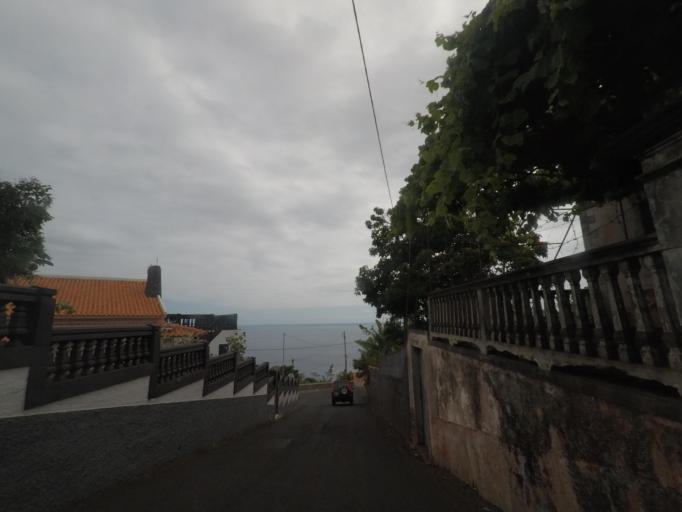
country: PT
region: Madeira
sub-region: Calheta
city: Arco da Calheta
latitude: 32.7124
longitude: -17.1504
